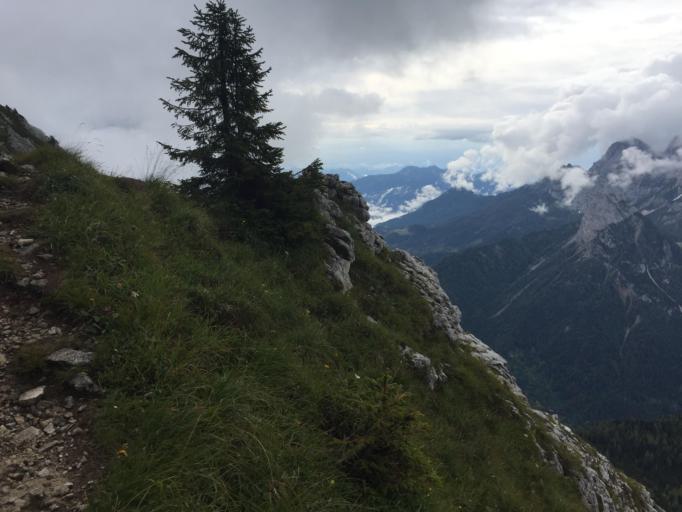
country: IT
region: Friuli Venezia Giulia
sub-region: Provincia di Udine
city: Forni Avoltri
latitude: 46.5950
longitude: 12.7367
